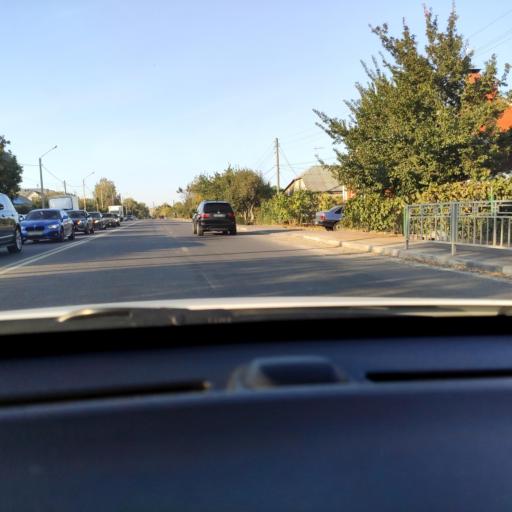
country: RU
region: Voronezj
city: Voronezh
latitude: 51.6943
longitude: 39.1574
